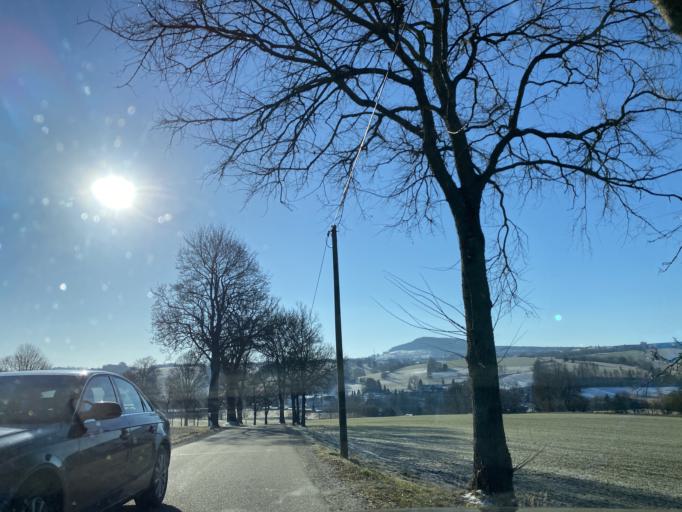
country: DE
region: Saxony
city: Wiesa
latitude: 50.6161
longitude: 13.0086
